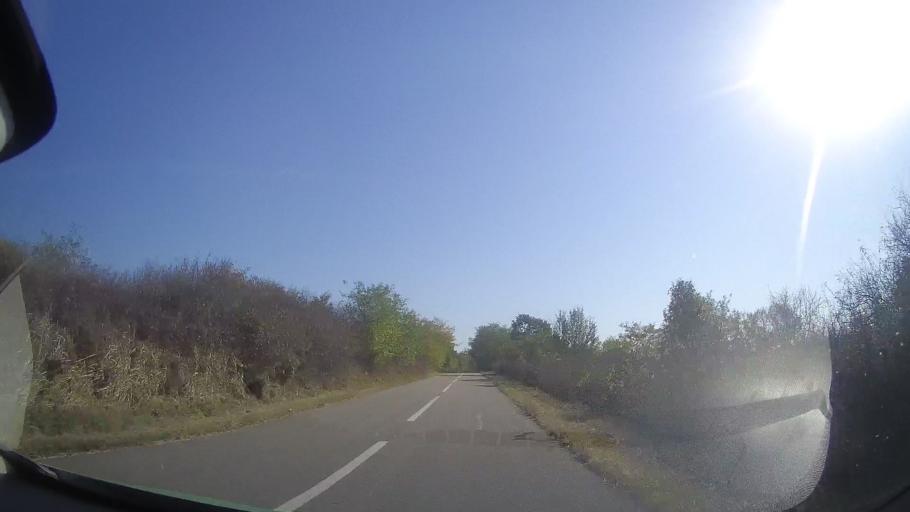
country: RO
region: Timis
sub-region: Comuna Ghizela
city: Ghizela
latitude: 45.8270
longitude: 21.7362
